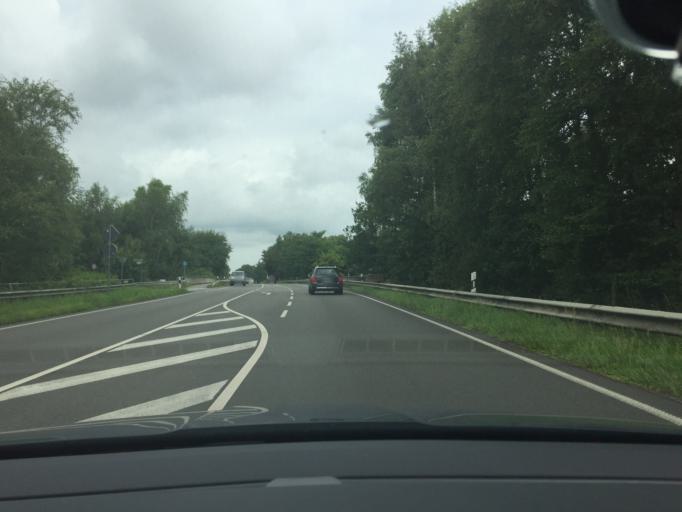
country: DE
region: Lower Saxony
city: Aurich
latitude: 53.4524
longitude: 7.5030
